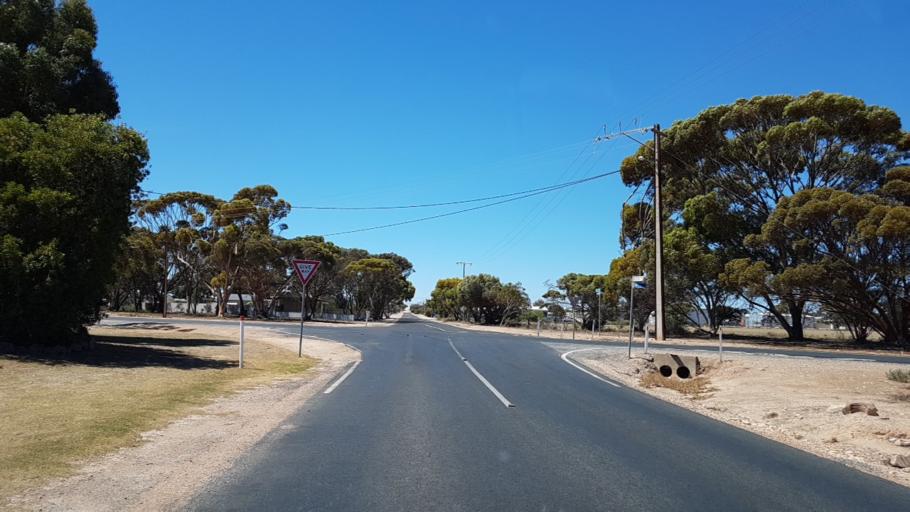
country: AU
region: South Australia
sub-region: Copper Coast
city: Wallaroo
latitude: -34.0617
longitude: 137.5928
